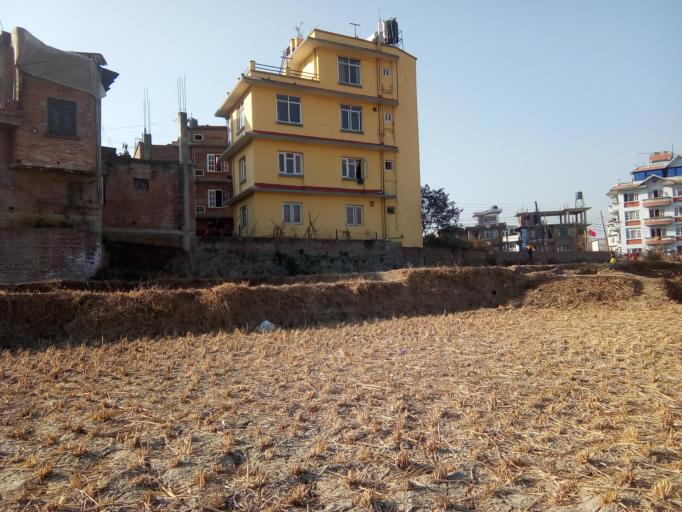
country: NP
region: Central Region
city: Kirtipur
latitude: 27.6755
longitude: 85.2746
